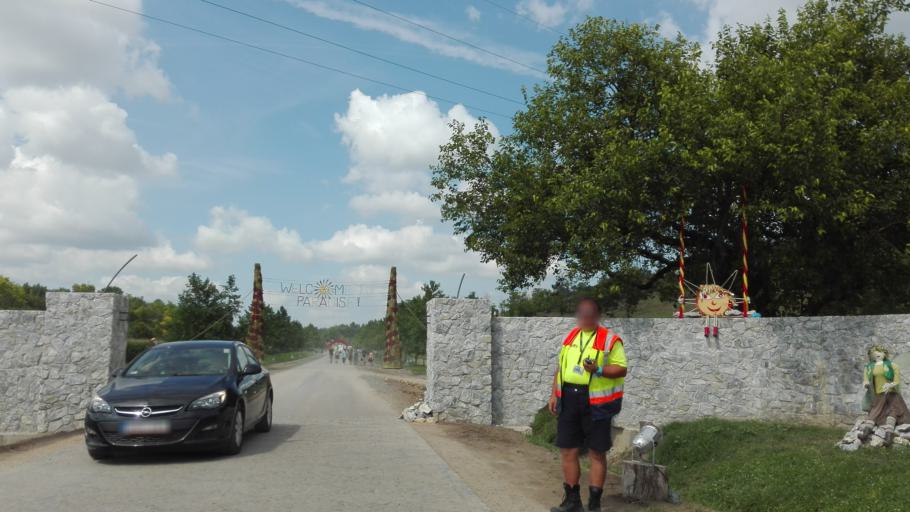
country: HU
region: Tolna
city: Ozora
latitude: 46.7552
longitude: 18.4349
